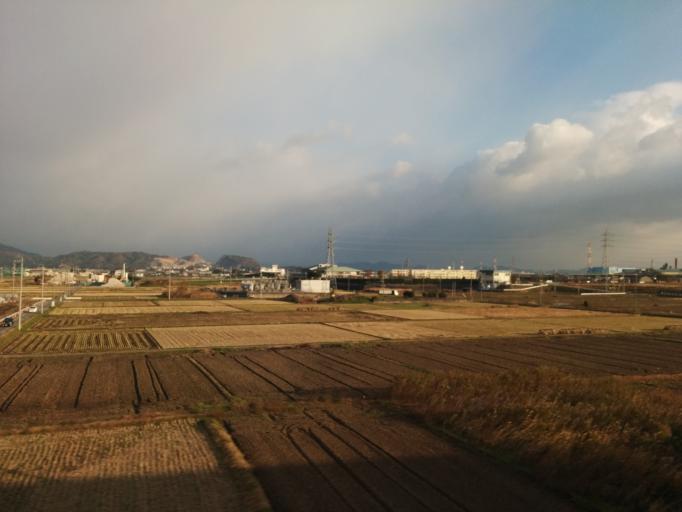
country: JP
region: Gifu
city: Tarui
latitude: 35.3493
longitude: 136.5728
